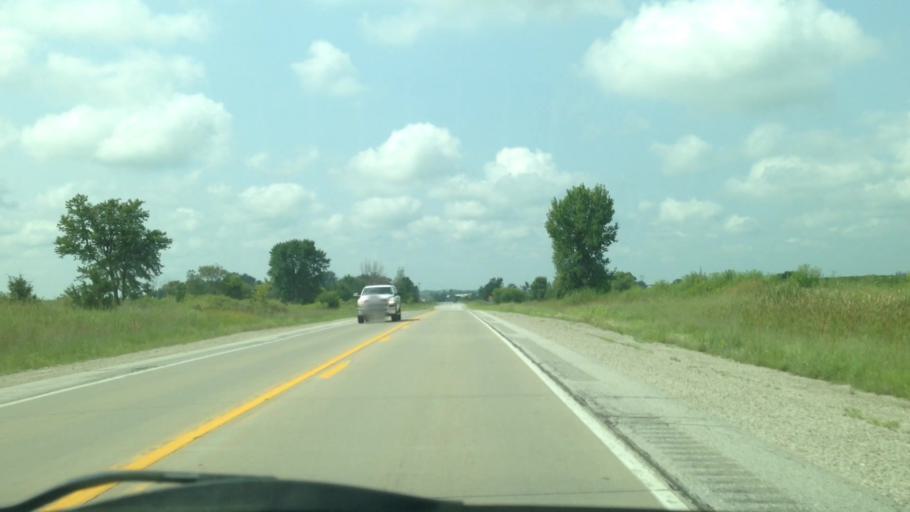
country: US
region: Iowa
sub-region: Benton County
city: Walford
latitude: 41.8977
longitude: -91.8075
